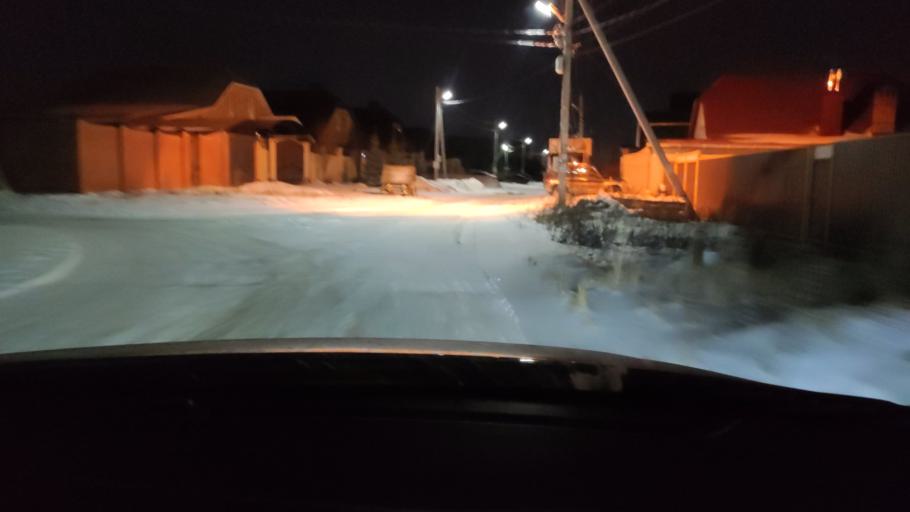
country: RU
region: Tatarstan
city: Vysokaya Gora
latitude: 55.8396
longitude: 49.2417
